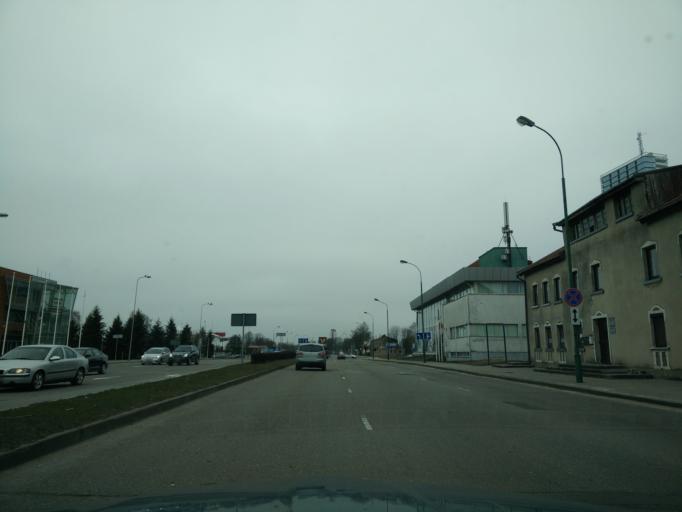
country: LT
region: Klaipedos apskritis
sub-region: Klaipeda
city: Klaipeda
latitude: 55.6879
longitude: 21.1458
